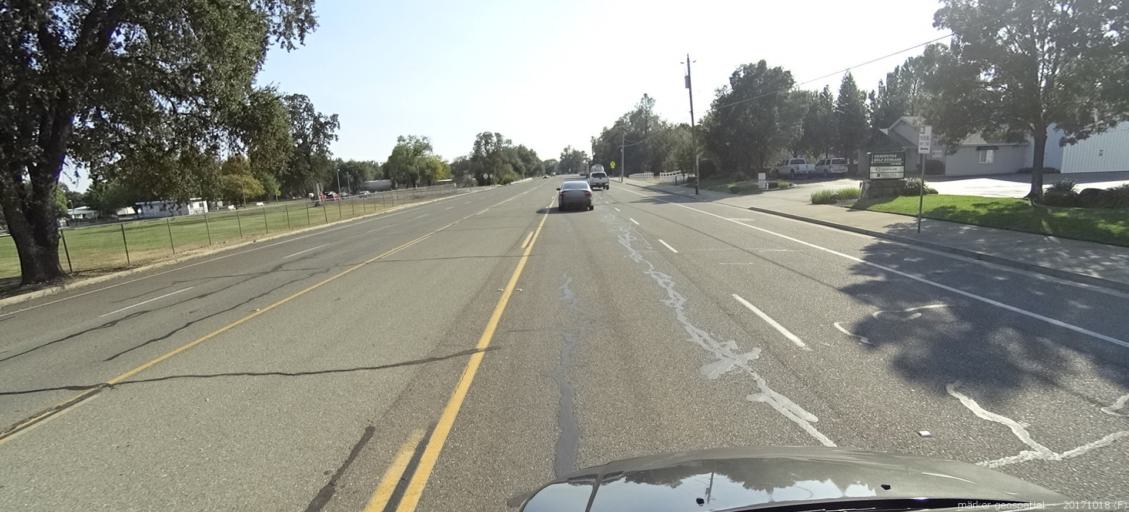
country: US
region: California
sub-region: Shasta County
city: Palo Cedro
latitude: 40.5514
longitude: -122.2384
